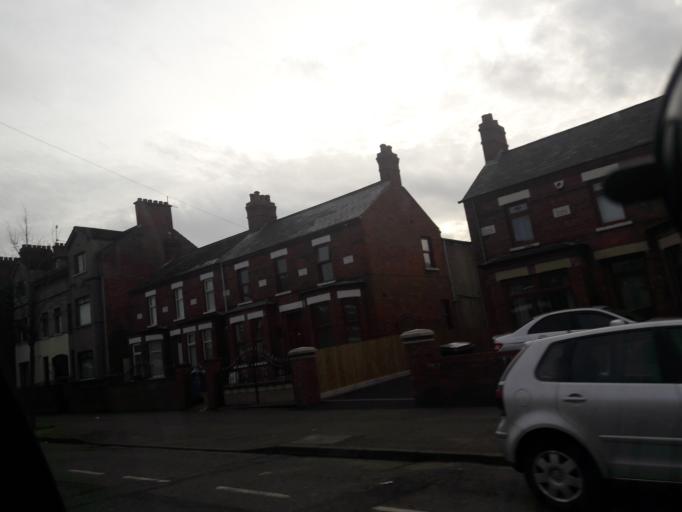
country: GB
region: Northern Ireland
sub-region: City of Belfast
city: Belfast
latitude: 54.6195
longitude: -5.9535
